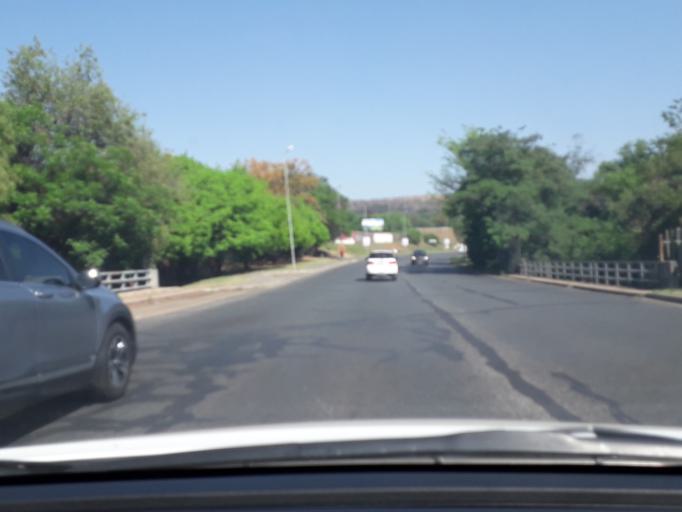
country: ZA
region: Gauteng
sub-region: City of Johannesburg Metropolitan Municipality
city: Roodepoort
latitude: -26.1008
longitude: 27.9678
